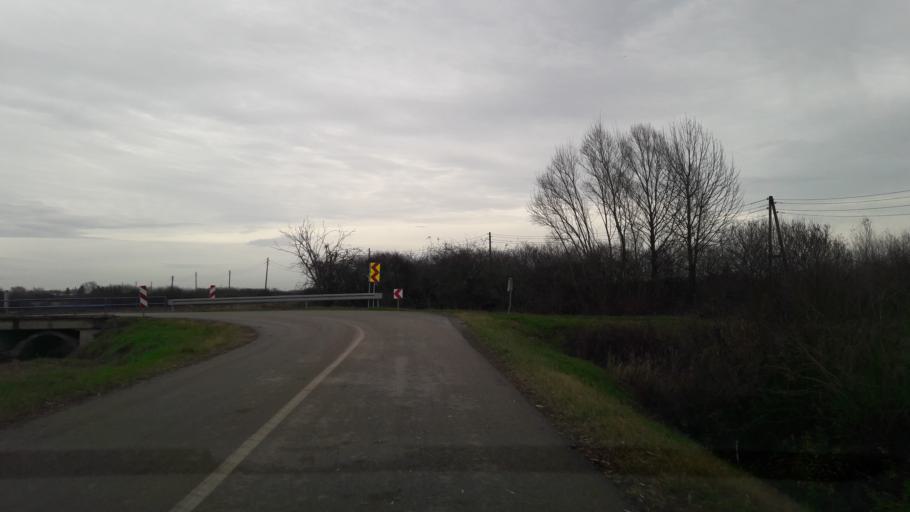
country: HR
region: Osjecko-Baranjska
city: Jelisavac
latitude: 45.6327
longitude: 18.1233
